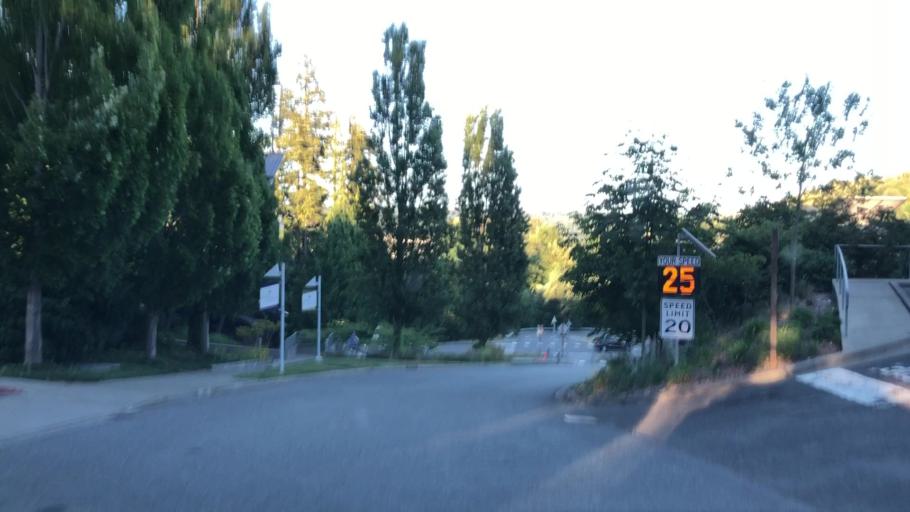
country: US
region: Washington
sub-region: King County
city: Bothell
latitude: 47.7583
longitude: -122.1918
